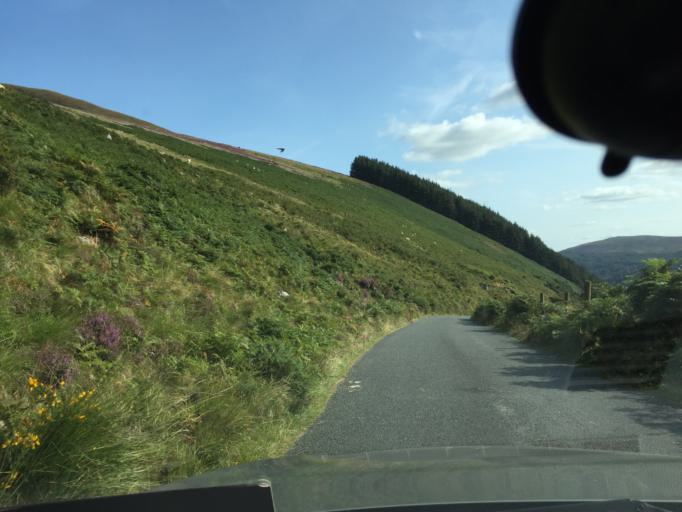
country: IE
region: Leinster
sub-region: Wicklow
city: Rathdrum
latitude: 53.0634
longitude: -6.3330
